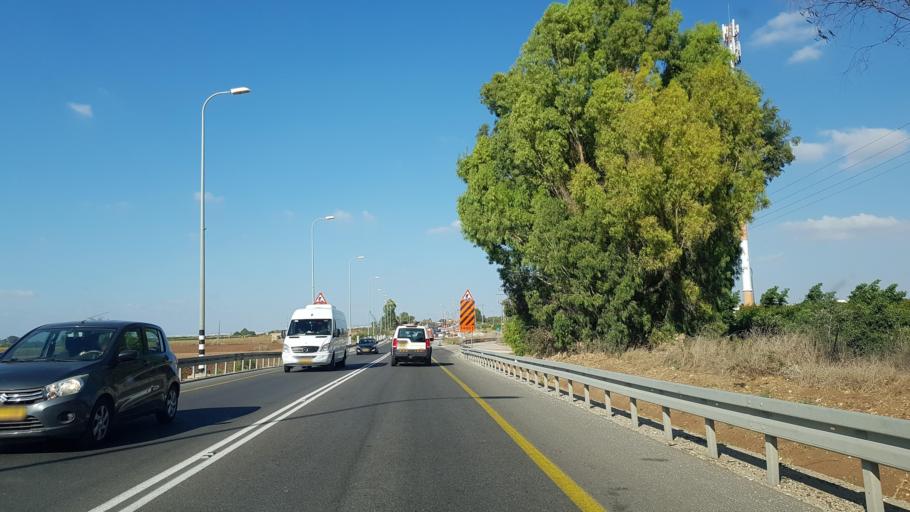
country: PS
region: West Bank
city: Tulkarm
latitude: 32.3322
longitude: 35.0051
